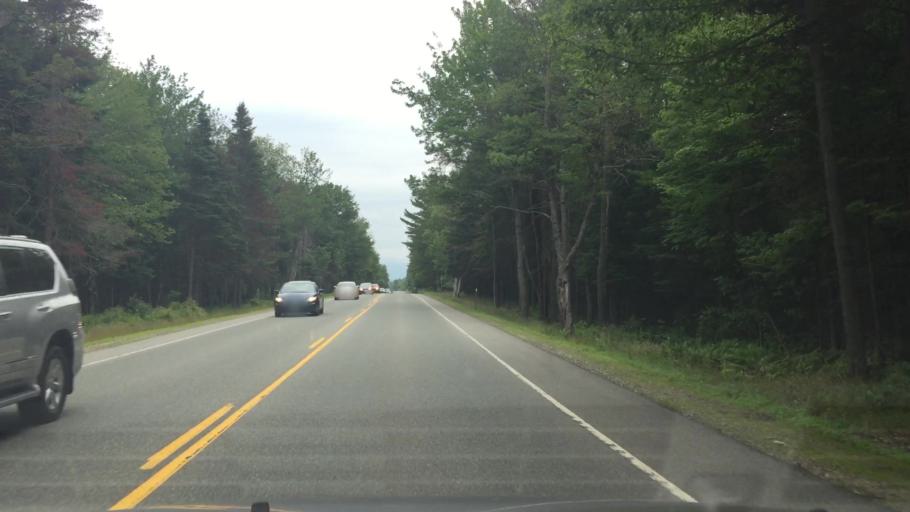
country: US
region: New Hampshire
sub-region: Grafton County
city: Deerfield
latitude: 44.2459
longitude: -71.6237
